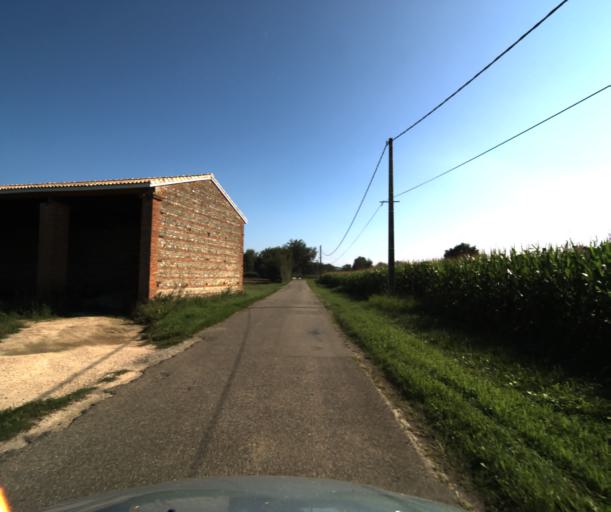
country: FR
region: Midi-Pyrenees
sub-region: Departement de la Haute-Garonne
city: Le Fauga
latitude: 43.4115
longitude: 1.3050
